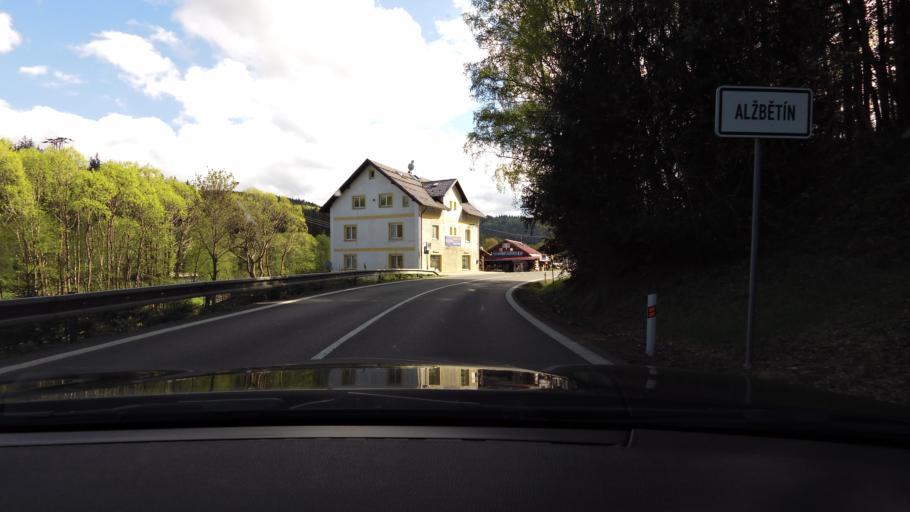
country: CZ
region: Plzensky
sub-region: Okres Klatovy
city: Zelezna Ruda
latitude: 49.1294
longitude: 13.2185
